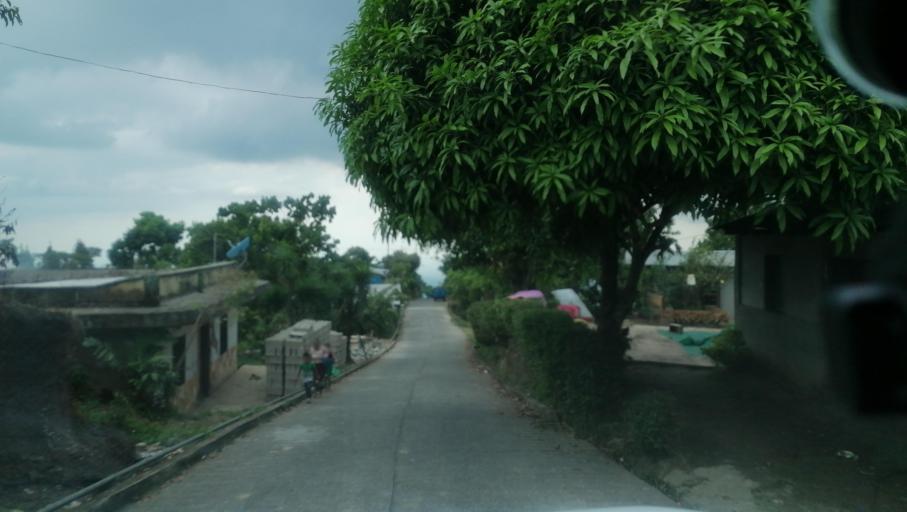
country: MX
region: Chiapas
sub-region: Cacahoatan
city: Benito Juarez
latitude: 15.0814
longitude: -92.1627
